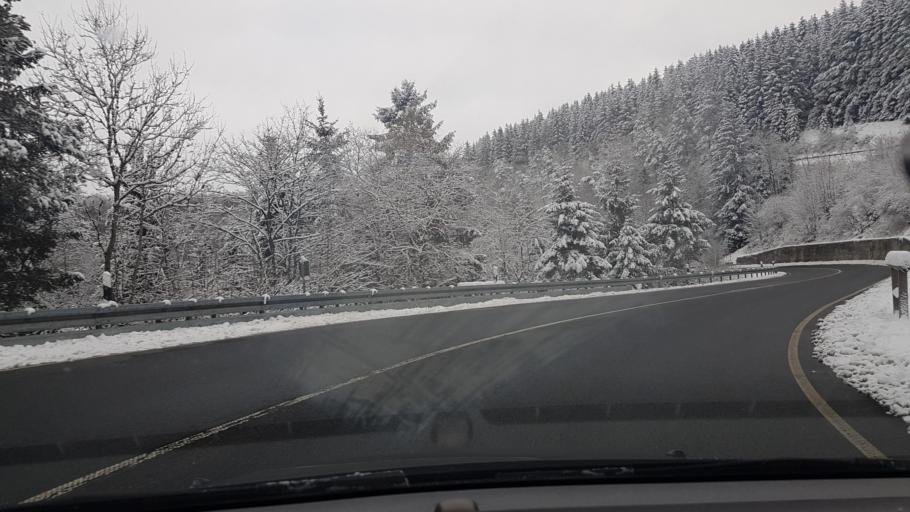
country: DE
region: Lower Saxony
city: Clausthal-Zellerfeld
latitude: 51.8047
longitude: 10.3060
